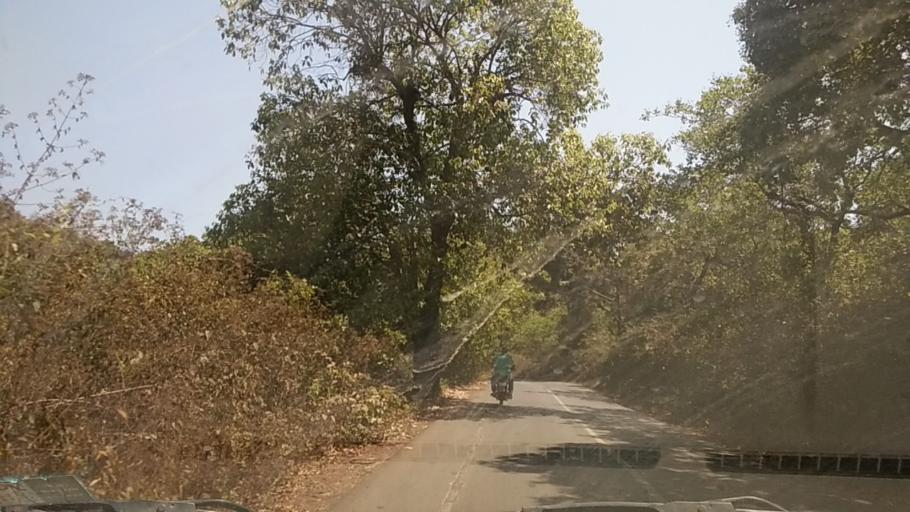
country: IN
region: Goa
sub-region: North Goa
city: Dicholi
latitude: 15.5821
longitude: 73.9346
